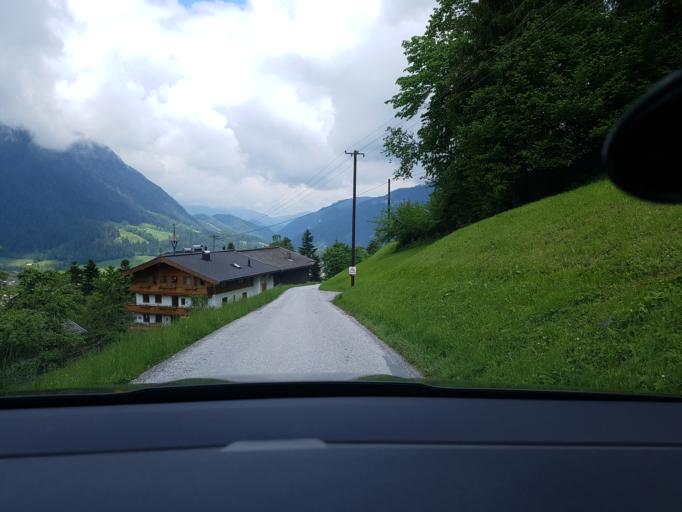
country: AT
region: Tyrol
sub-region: Politischer Bezirk Kufstein
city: Soll
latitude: 47.4929
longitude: 12.2018
